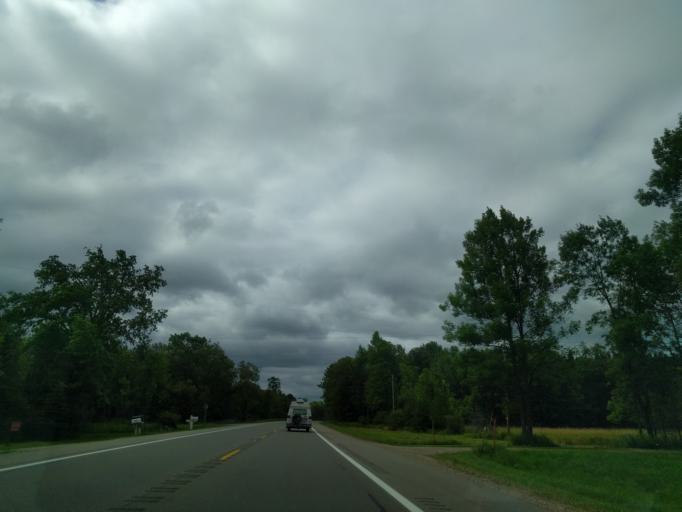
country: US
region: Michigan
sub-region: Menominee County
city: Menominee
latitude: 45.2679
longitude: -87.4708
